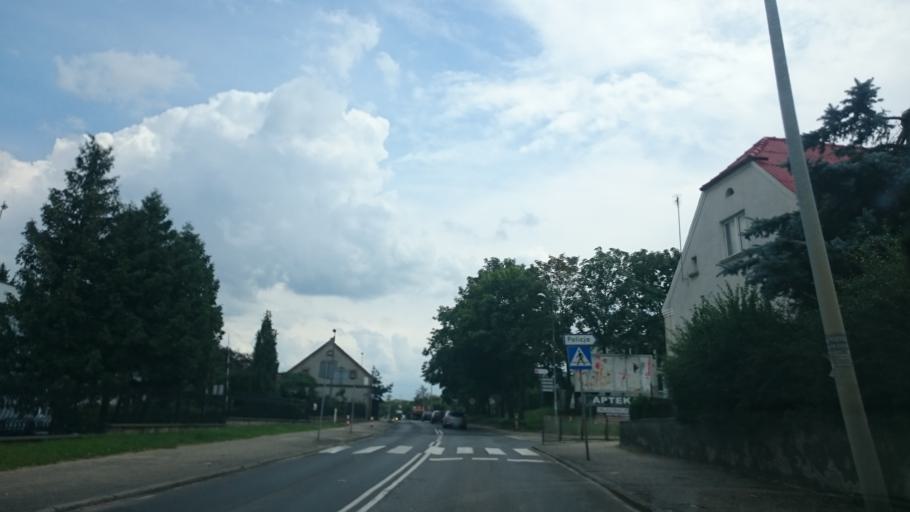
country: PL
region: Kujawsko-Pomorskie
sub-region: Powiat tucholski
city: Tuchola
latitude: 53.5895
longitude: 17.8666
